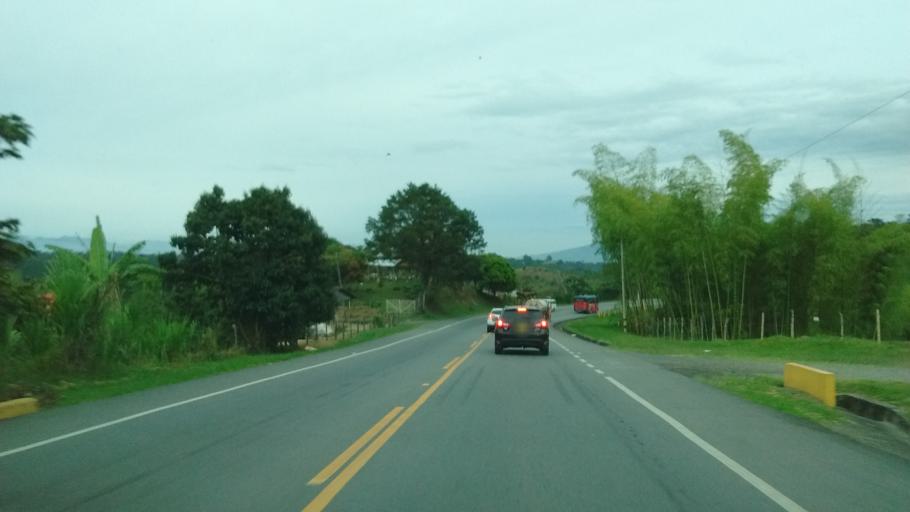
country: CO
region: Cauca
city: Morales
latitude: 2.7702
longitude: -76.5550
